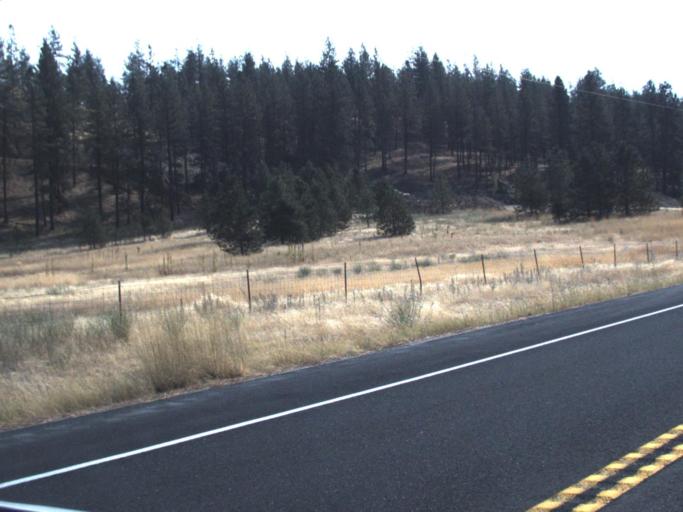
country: US
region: Washington
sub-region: Spokane County
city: Fairwood
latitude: 47.7618
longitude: -117.5366
